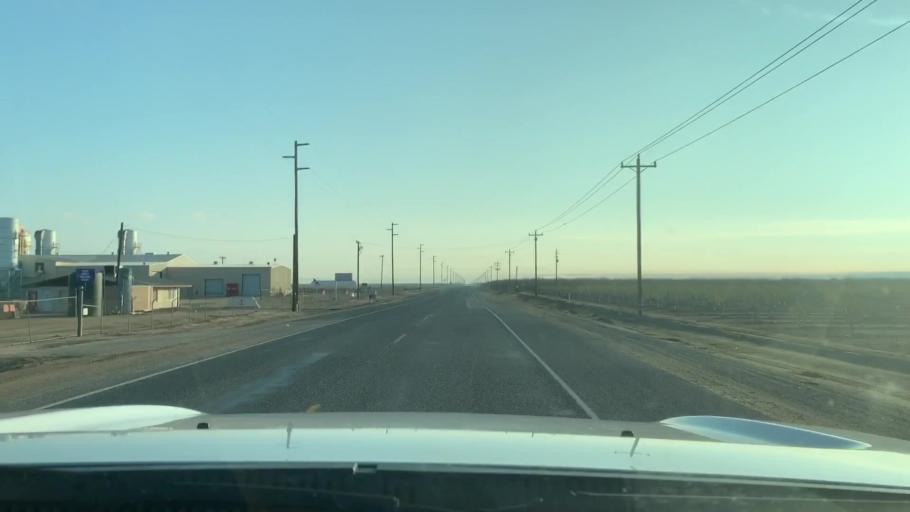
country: US
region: California
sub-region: Kern County
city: Wasco
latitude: 35.6010
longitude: -119.5025
